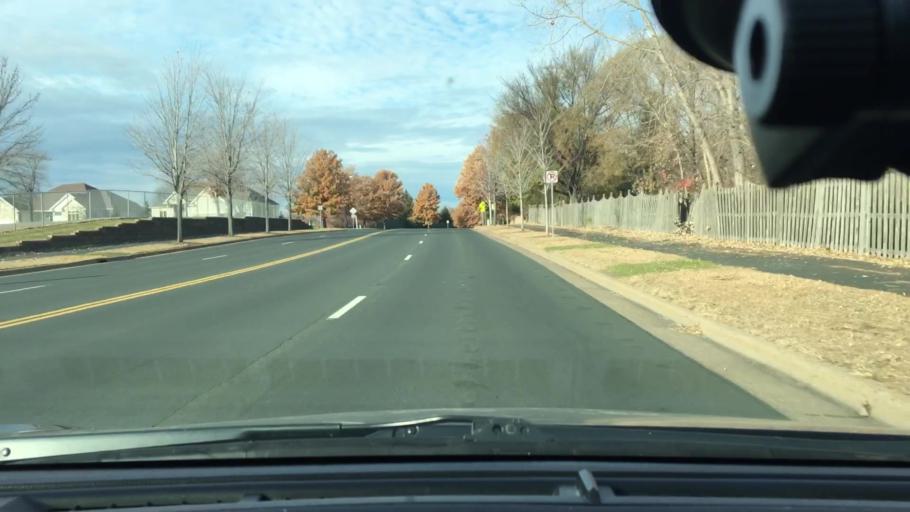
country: US
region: Minnesota
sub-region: Hennepin County
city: Maple Grove
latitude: 45.1027
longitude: -93.4736
